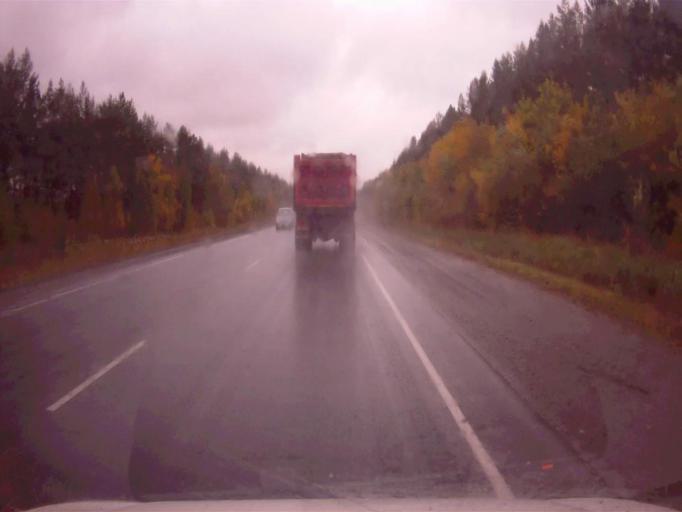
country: RU
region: Chelyabinsk
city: Roshchino
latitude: 55.3583
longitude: 61.2333
